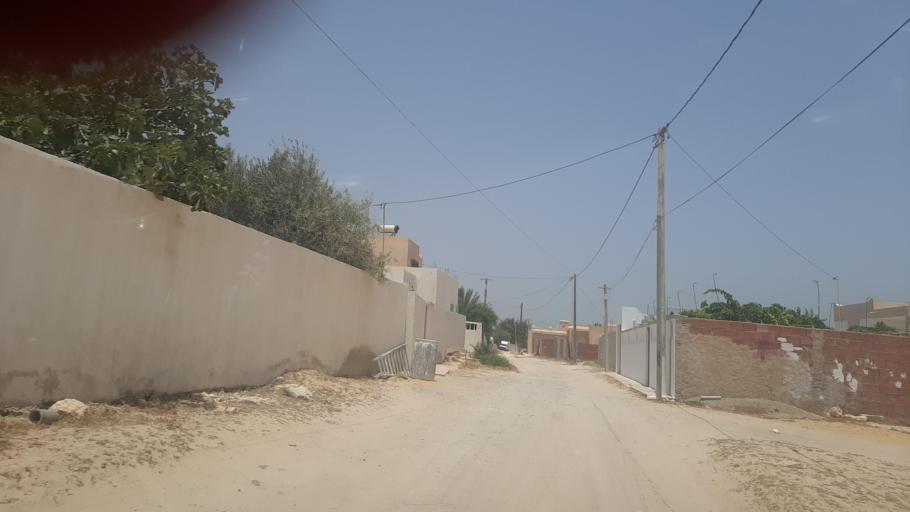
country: TN
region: Safaqis
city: Al Qarmadah
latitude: 34.6520
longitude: 11.0257
